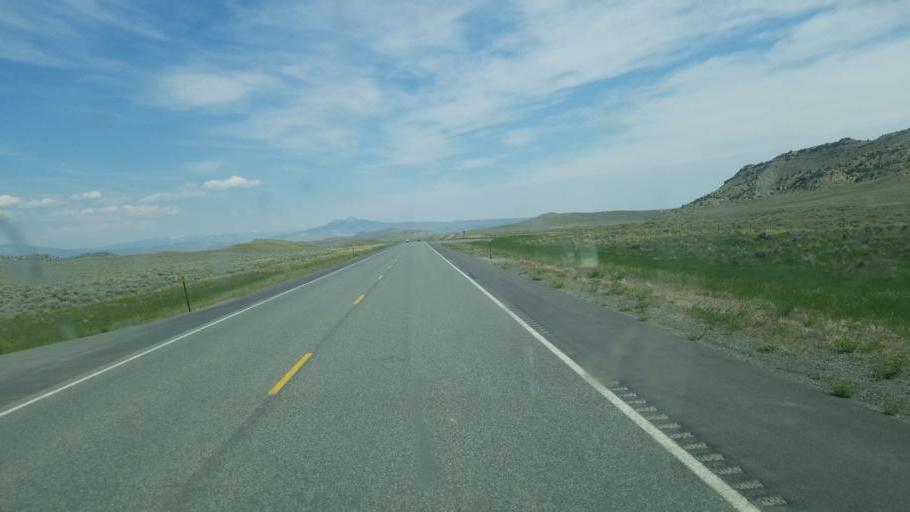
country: US
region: Wyoming
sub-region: Park County
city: Cody
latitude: 44.4121
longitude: -109.0072
